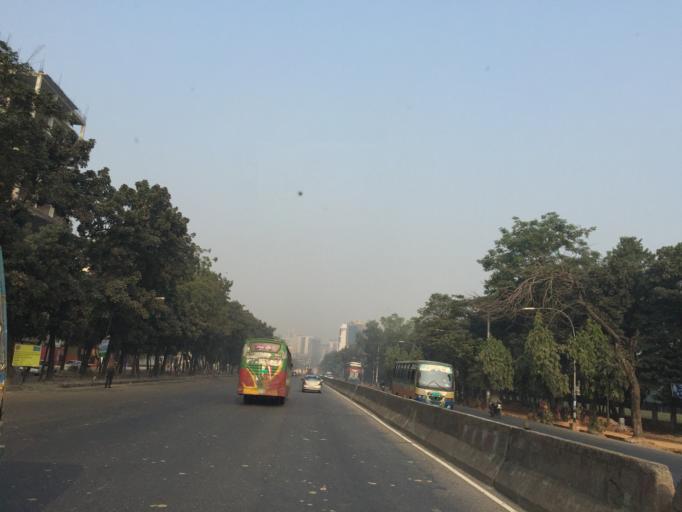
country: BD
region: Dhaka
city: Tungi
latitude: 23.8552
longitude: 90.4046
